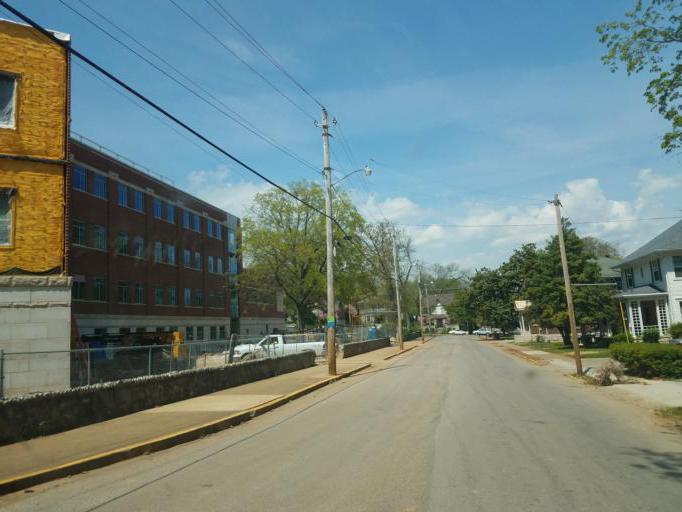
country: US
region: Kentucky
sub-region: Warren County
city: Bowling Green
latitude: 36.9867
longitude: -86.4475
